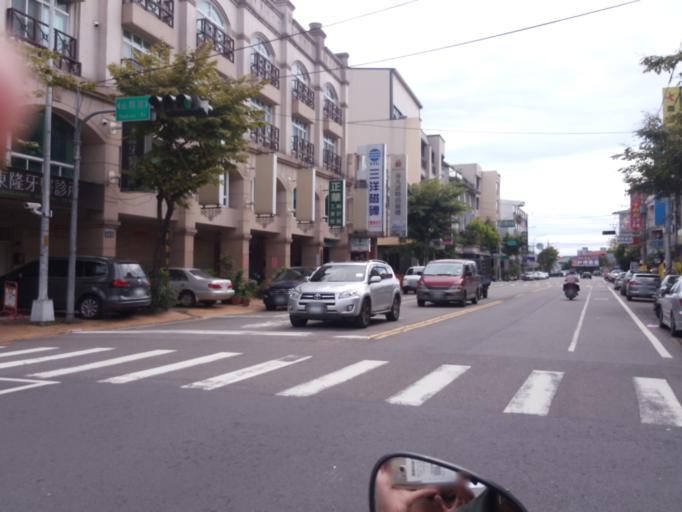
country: TW
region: Taiwan
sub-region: Taichung City
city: Taichung
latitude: 24.1094
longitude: 120.6766
